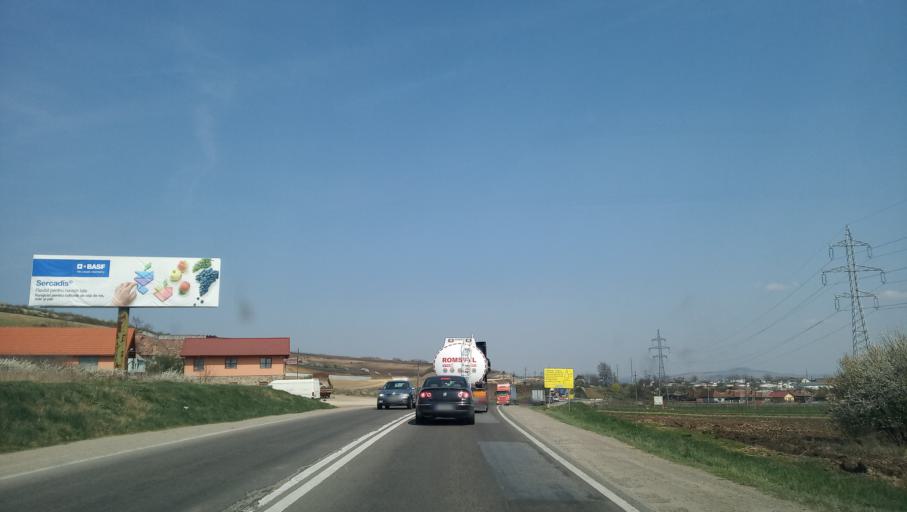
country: RO
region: Alba
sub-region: Comuna Santimbru
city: Santimbru
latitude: 46.1340
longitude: 23.6309
